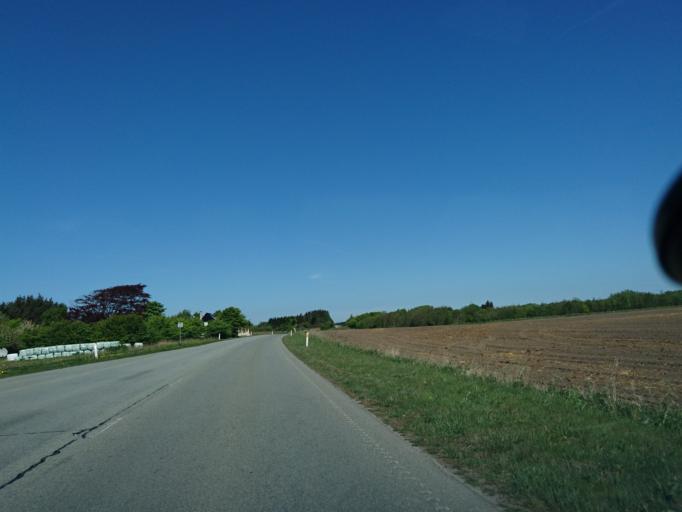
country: DK
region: North Denmark
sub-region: Hjorring Kommune
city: Hjorring
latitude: 57.4906
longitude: 10.0010
